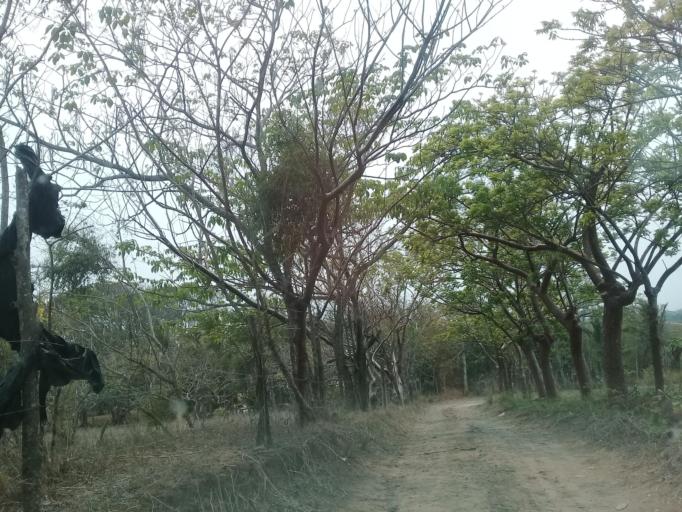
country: MX
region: Veracruz
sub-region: Medellin
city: La Laguna y Monte del Castillo
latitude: 18.9585
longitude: -96.1223
